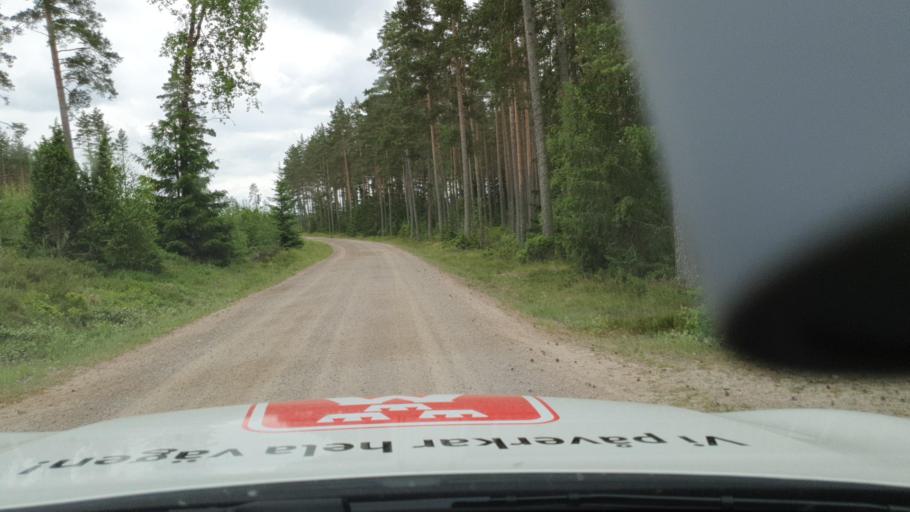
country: SE
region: Vaestra Goetaland
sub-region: Tidaholms Kommun
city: Olofstorp
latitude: 58.1971
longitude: 14.1087
